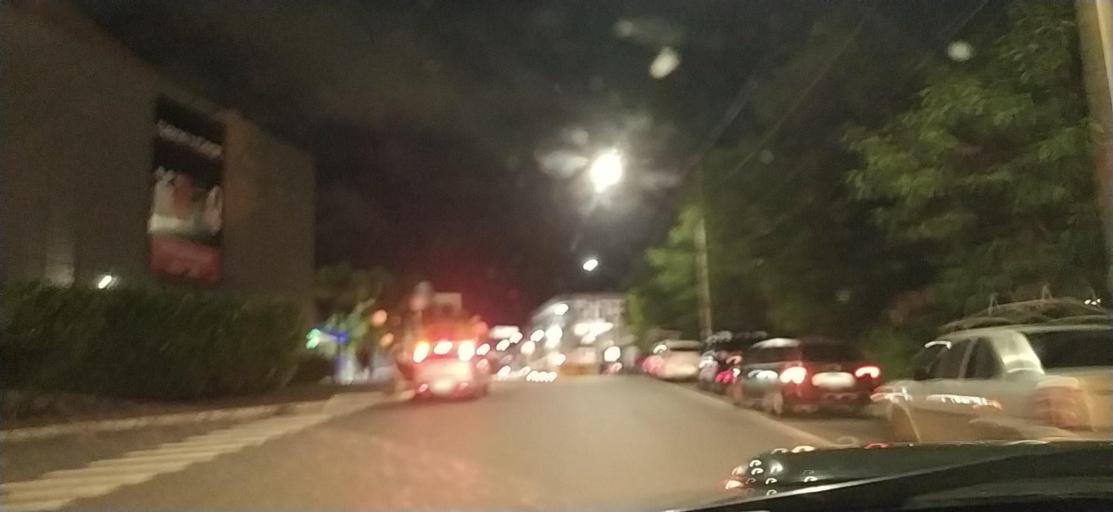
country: BR
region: Sao Paulo
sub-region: Hortolandia
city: Hortolandia
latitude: -22.8634
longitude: -47.2141
